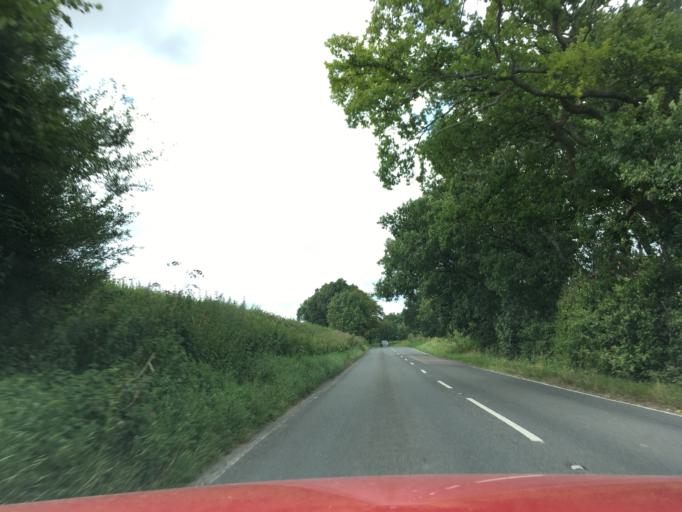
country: GB
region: England
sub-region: Kent
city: Tenterden
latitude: 51.0494
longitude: 0.7350
